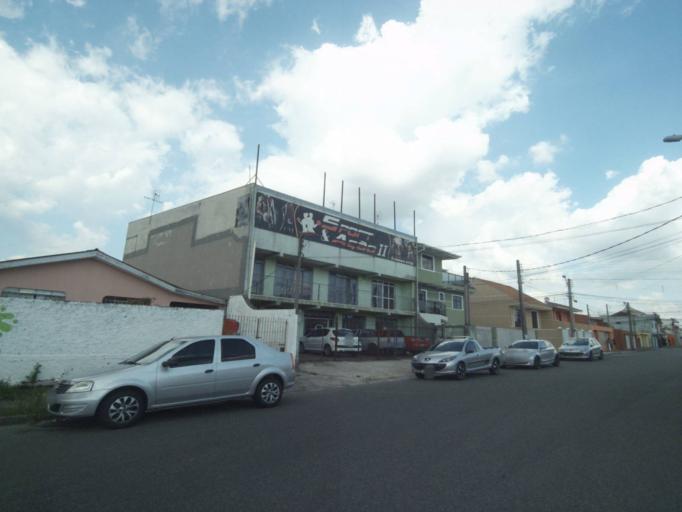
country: BR
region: Parana
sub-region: Sao Jose Dos Pinhais
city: Sao Jose dos Pinhais
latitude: -25.5305
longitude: -49.2622
